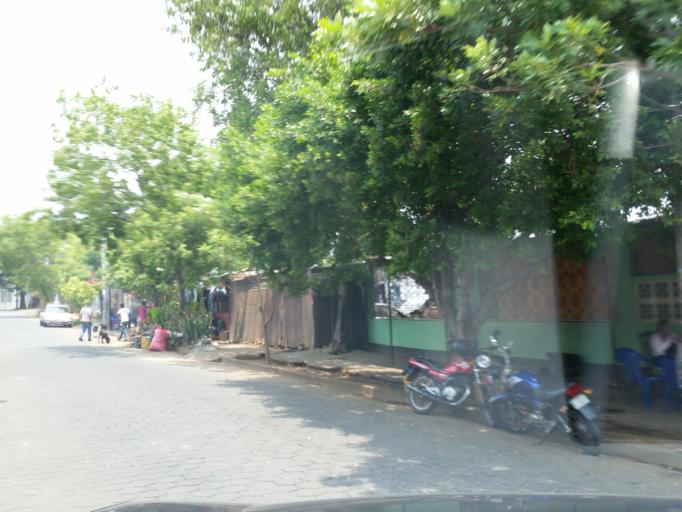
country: NI
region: Managua
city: Managua
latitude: 12.1500
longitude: -86.2303
